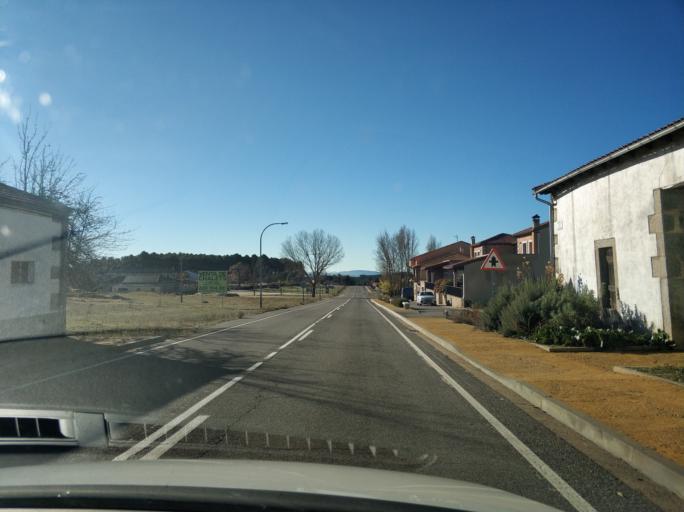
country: ES
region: Castille and Leon
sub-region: Provincia de Salamanca
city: San Miguel de Valero
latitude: 40.5432
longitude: -5.9194
